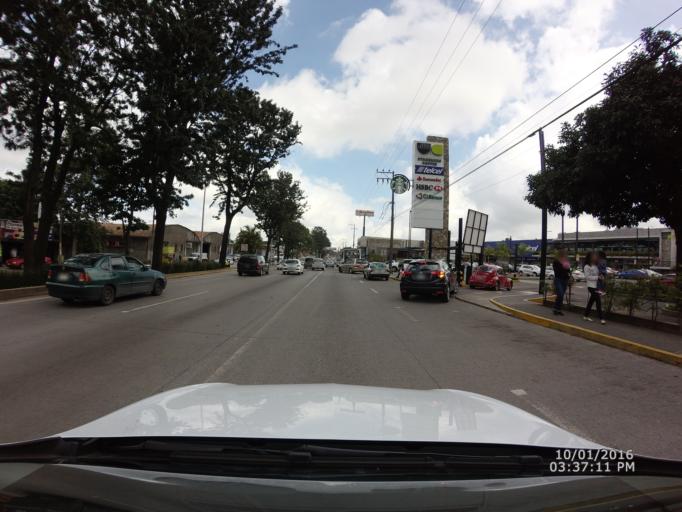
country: MX
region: Veracruz
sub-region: Xalapa
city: Xalapa de Enriquez
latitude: 19.5605
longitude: -96.9239
